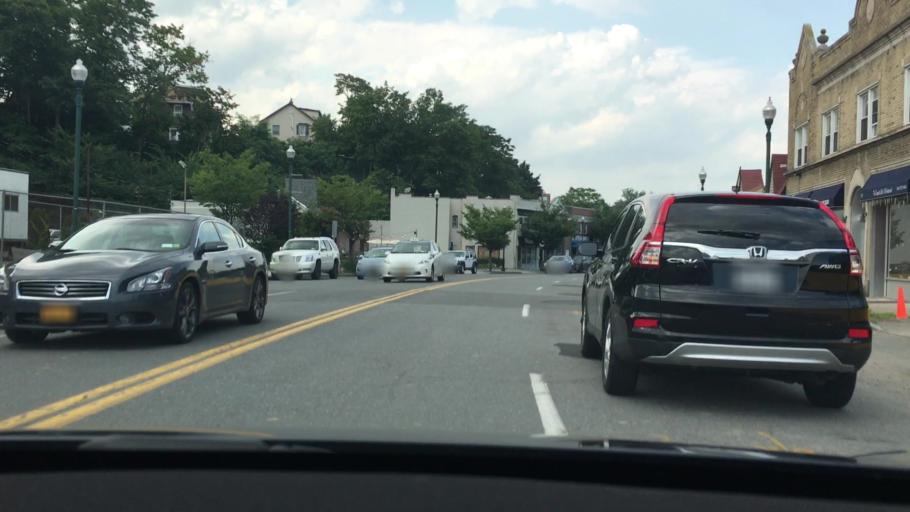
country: US
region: New York
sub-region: Westchester County
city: New Rochelle
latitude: 40.9221
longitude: -73.7881
